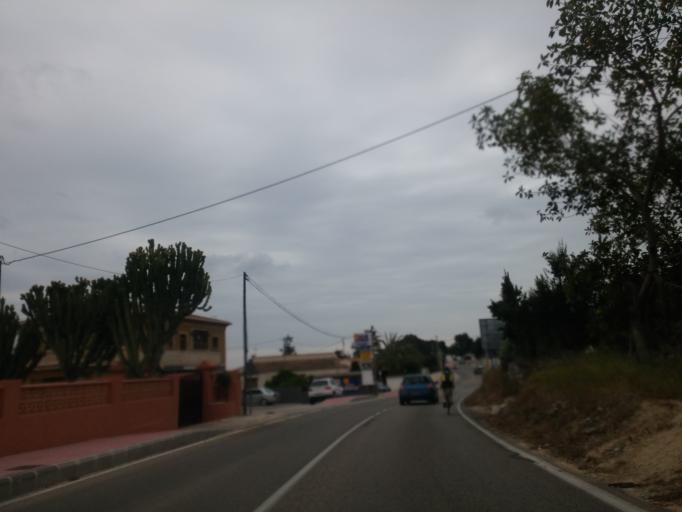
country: ES
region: Valencia
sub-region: Provincia de Alicante
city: Calp
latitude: 38.6642
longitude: 0.0850
